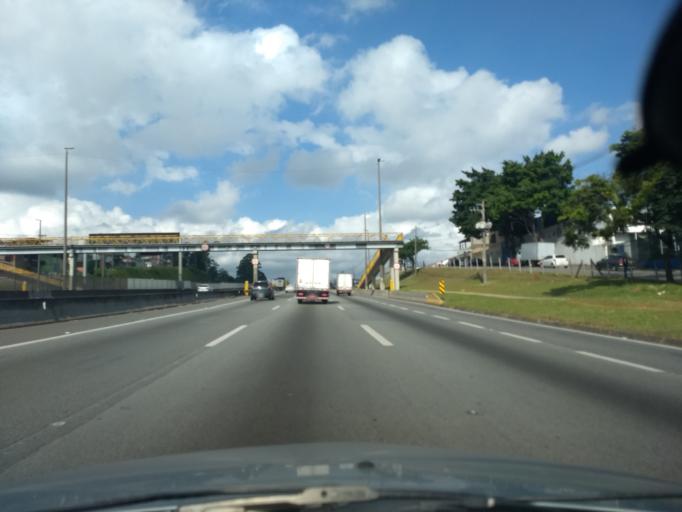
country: BR
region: Sao Paulo
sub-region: Itaquaquecetuba
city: Itaquaquecetuba
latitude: -23.4352
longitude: -46.4258
